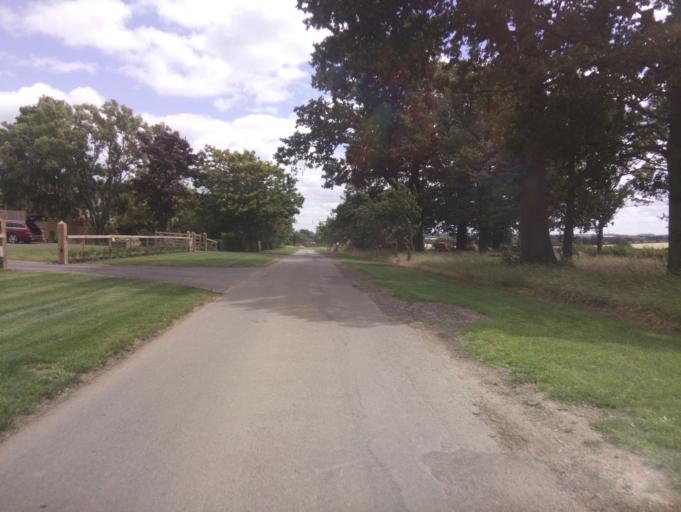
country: GB
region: England
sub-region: Nottinghamshire
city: Cotgrave
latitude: 52.8569
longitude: -1.0500
